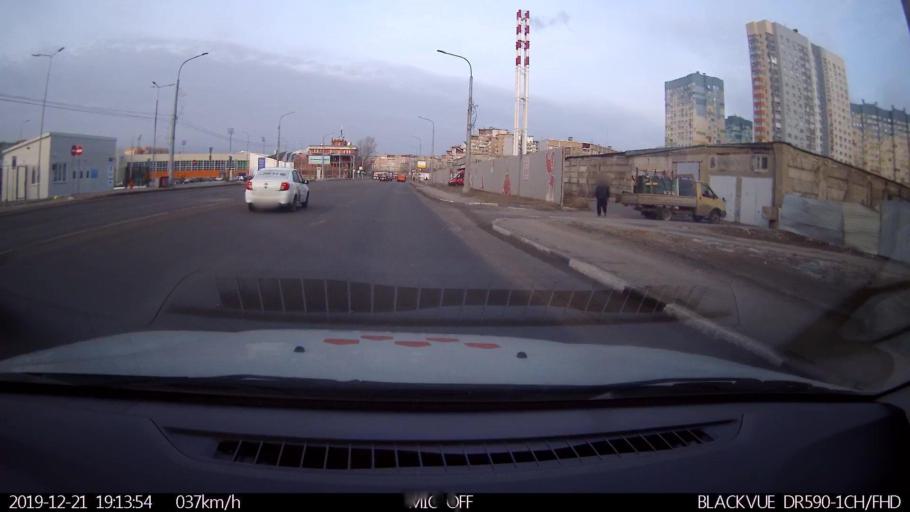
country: RU
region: Nizjnij Novgorod
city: Nizhniy Novgorod
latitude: 56.3389
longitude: 43.9463
